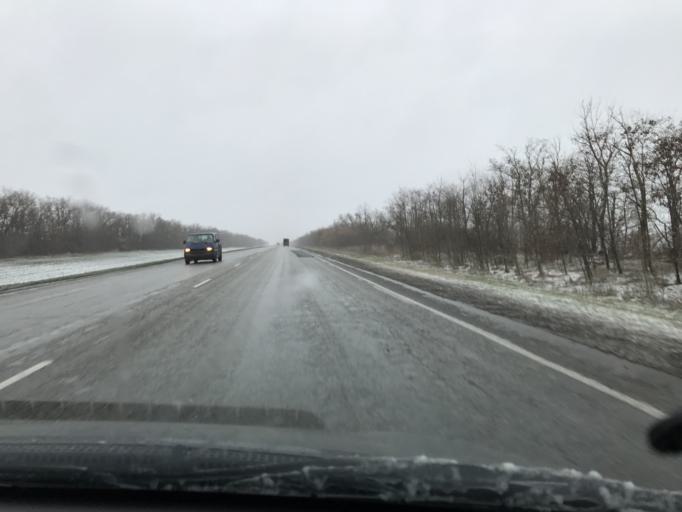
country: RU
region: Rostov
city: Mechetinskaya
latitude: 46.7396
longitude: 40.4711
